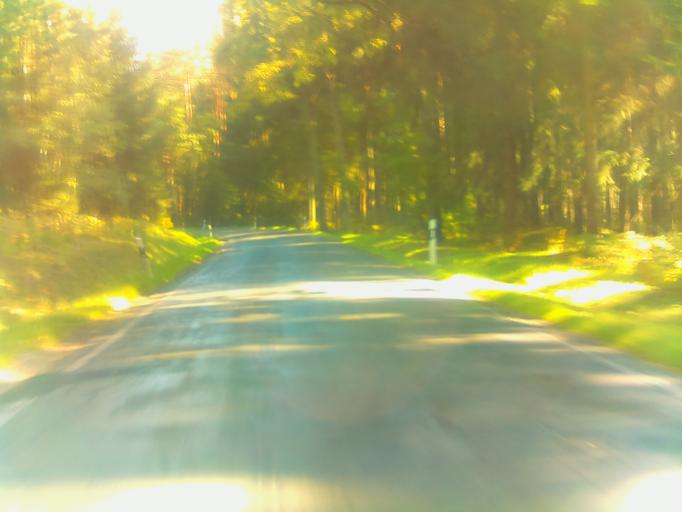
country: DE
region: Thuringia
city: Oberbodnitz
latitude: 50.7930
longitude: 11.6678
